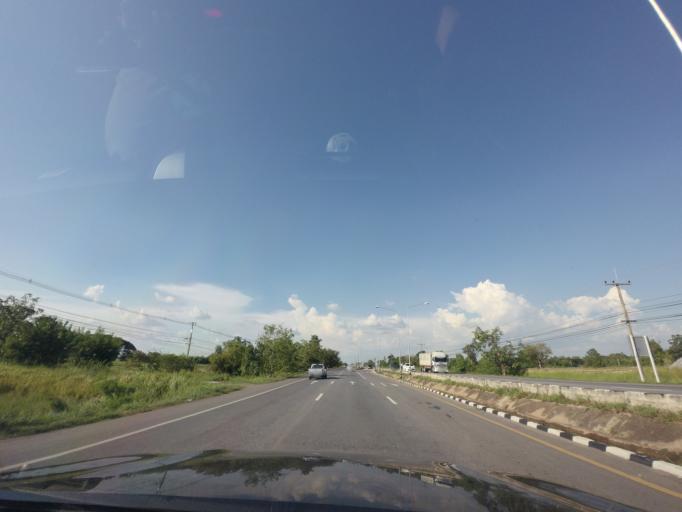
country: TH
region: Khon Kaen
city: Non Sila
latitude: 15.9829
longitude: 102.6964
